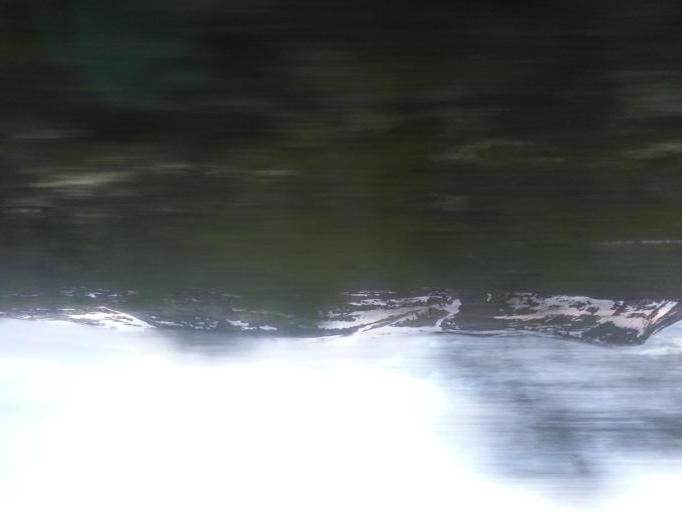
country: NO
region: Oppland
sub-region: Dovre
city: Dovre
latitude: 62.1650
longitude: 9.3552
